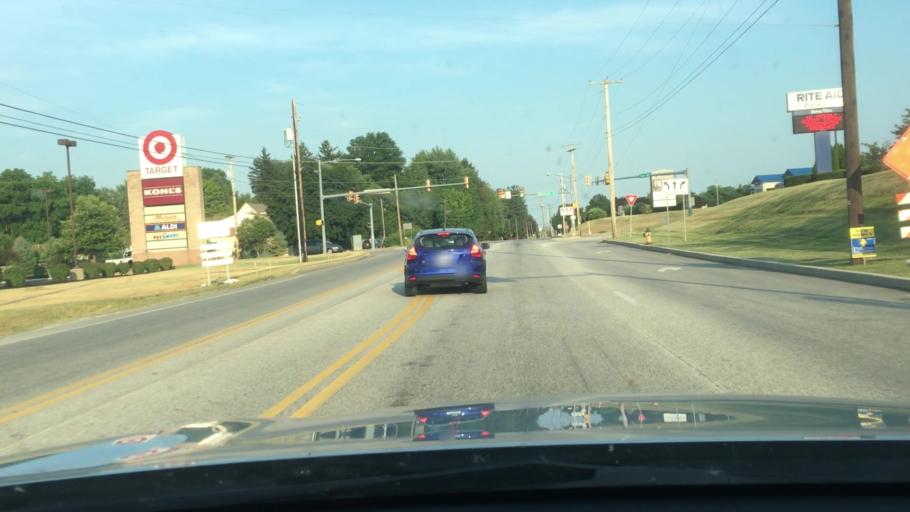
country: US
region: Pennsylvania
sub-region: Cumberland County
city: Carlisle
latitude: 40.1920
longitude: -77.1613
